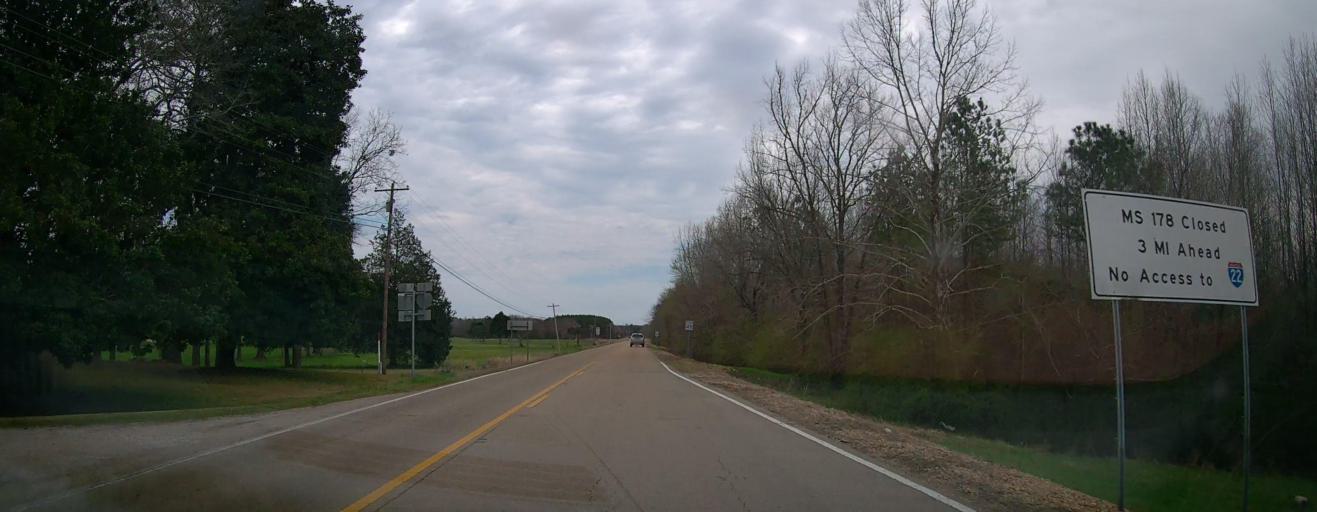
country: US
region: Mississippi
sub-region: Itawamba County
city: Fulton
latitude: 34.2339
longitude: -88.2559
